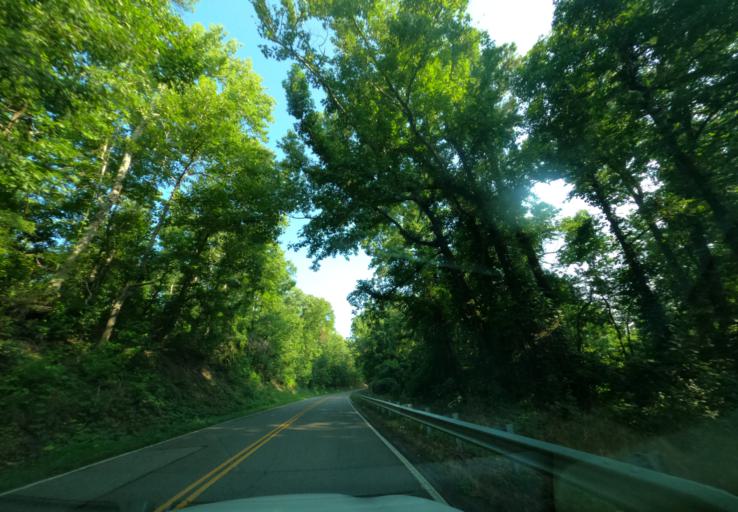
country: US
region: South Carolina
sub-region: Edgefield County
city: Murphys Estates
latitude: 33.6247
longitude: -81.9723
